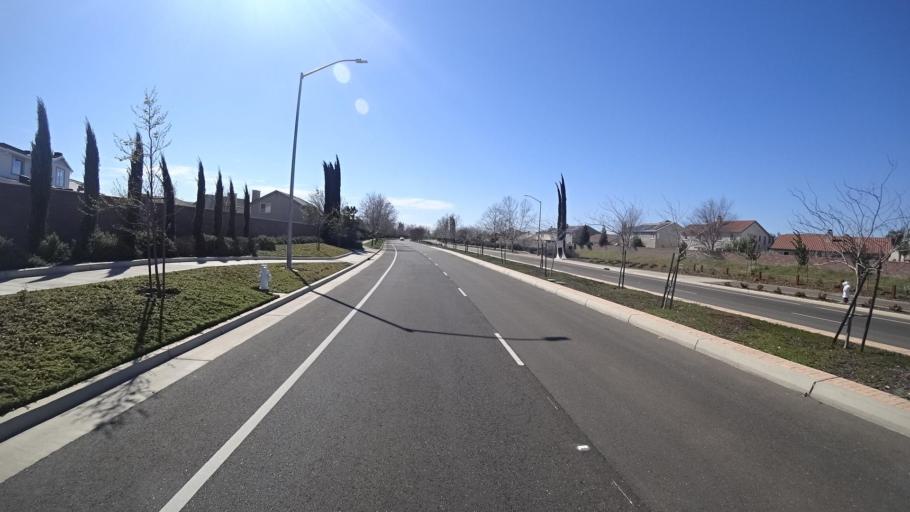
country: US
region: California
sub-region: Sacramento County
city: Gold River
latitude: 38.5497
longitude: -121.2335
